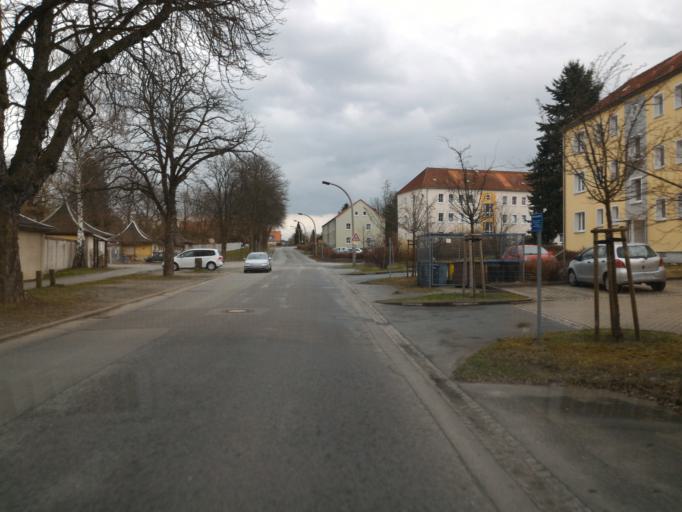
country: DE
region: Saxony
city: Neugersdorf
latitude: 50.9834
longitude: 14.6185
